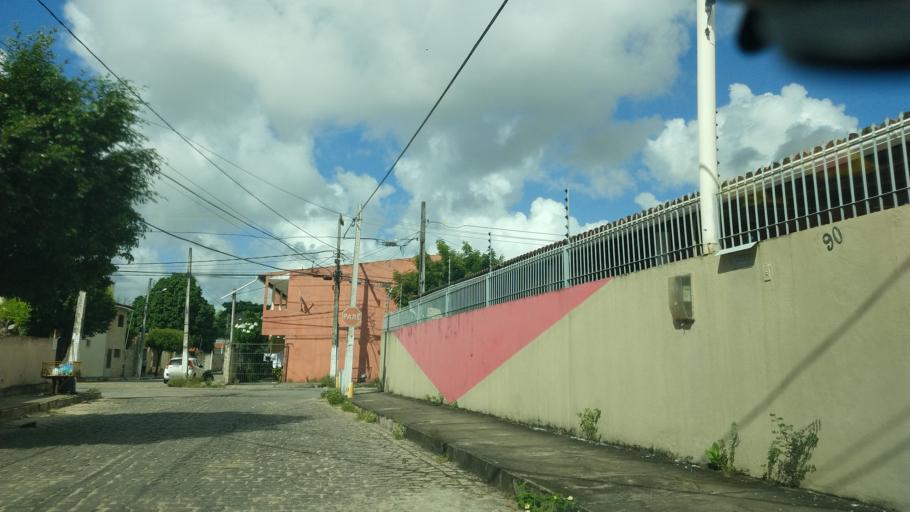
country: BR
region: Rio Grande do Norte
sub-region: Natal
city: Natal
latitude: -5.8616
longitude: -35.2082
